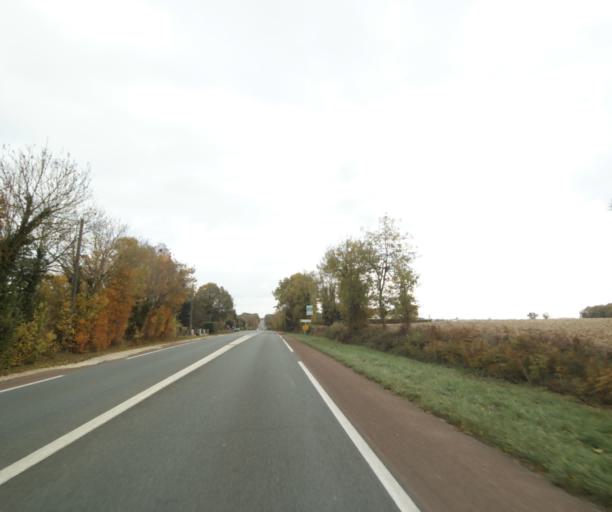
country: FR
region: Poitou-Charentes
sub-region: Departement de la Charente-Maritime
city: Saint-Georges-des-Coteaux
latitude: 45.7660
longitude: -0.6781
